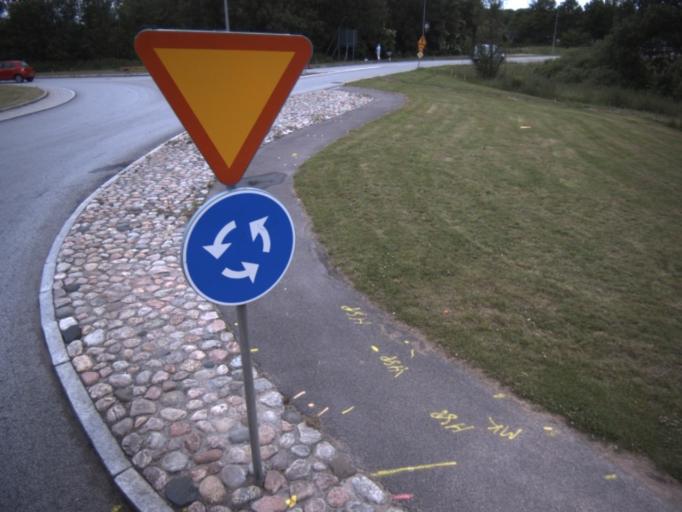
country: SE
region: Skane
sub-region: Helsingborg
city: Odakra
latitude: 56.0809
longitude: 12.7318
